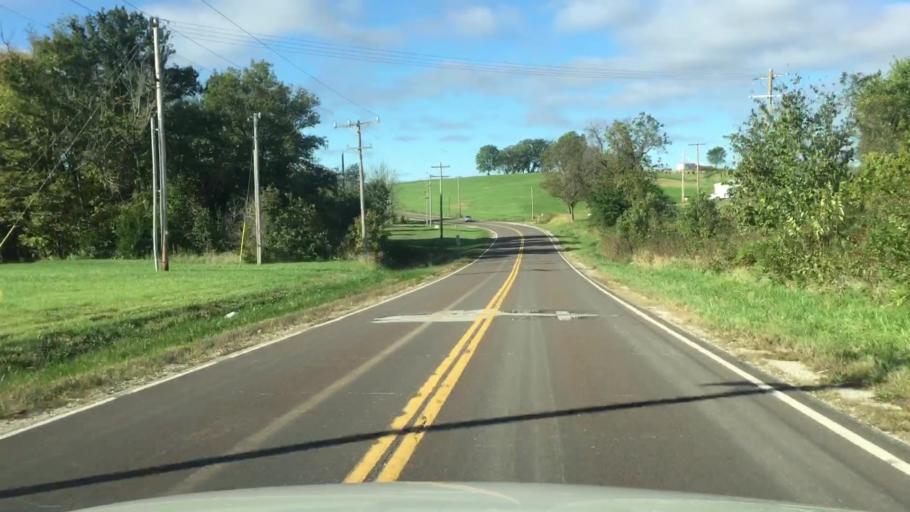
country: US
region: Missouri
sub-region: Howard County
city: Fayette
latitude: 39.1118
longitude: -92.7277
